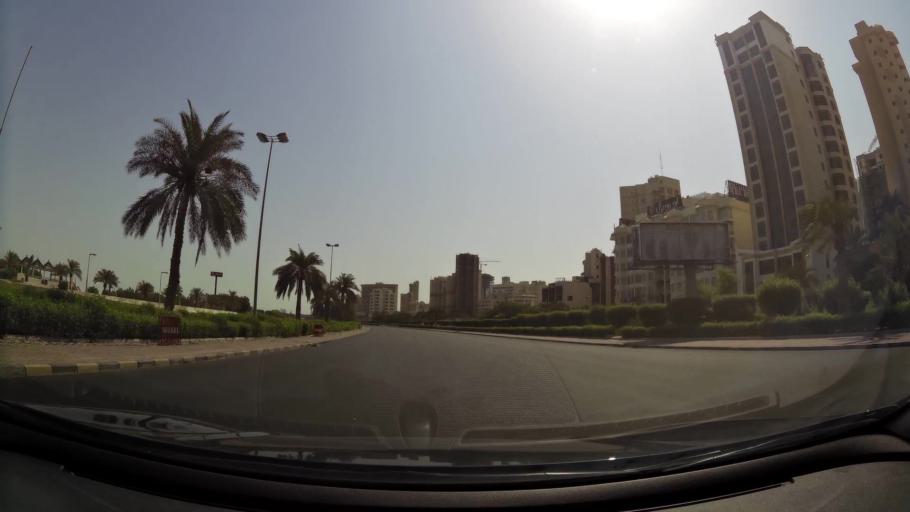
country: KW
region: Al Asimah
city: Ad Dasmah
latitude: 29.3742
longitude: 48.0056
